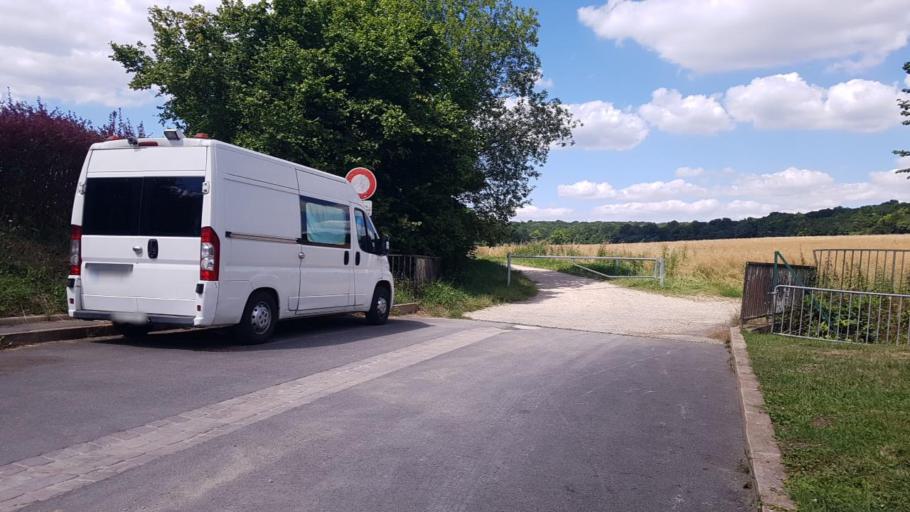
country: FR
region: Ile-de-France
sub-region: Departement de Seine-et-Marne
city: Moussy-le-Vieux
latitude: 49.0507
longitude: 2.6234
